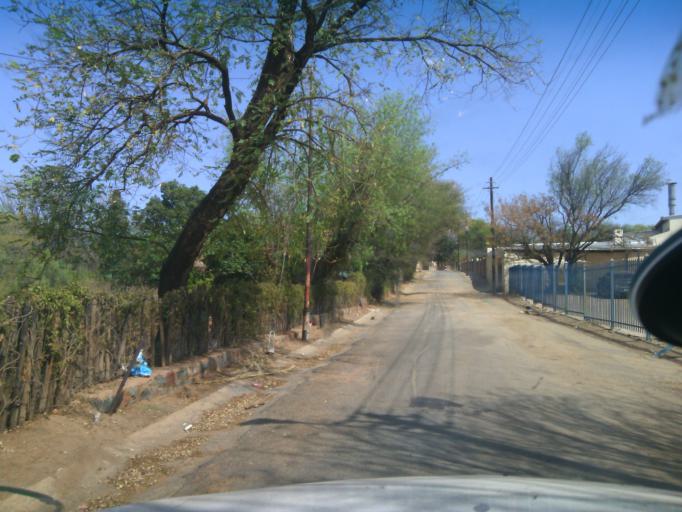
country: ZA
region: Northern Cape
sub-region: Frances Baard District Municipality
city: Barkly West
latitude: -28.5385
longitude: 24.5212
